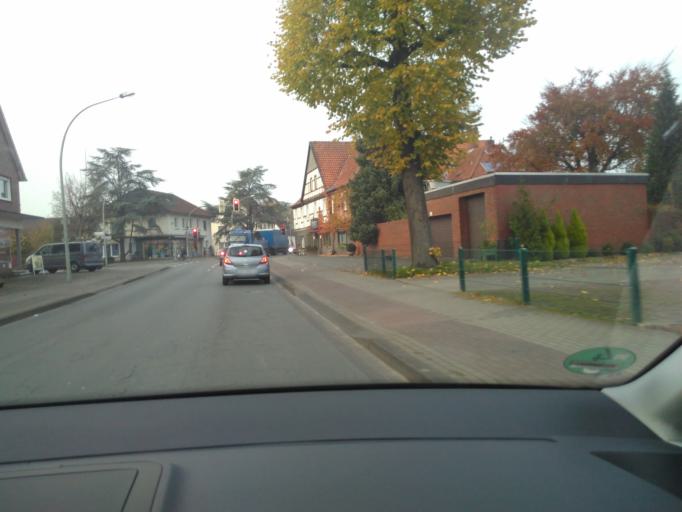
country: DE
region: North Rhine-Westphalia
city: Rietberg
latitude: 51.8329
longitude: 8.4453
